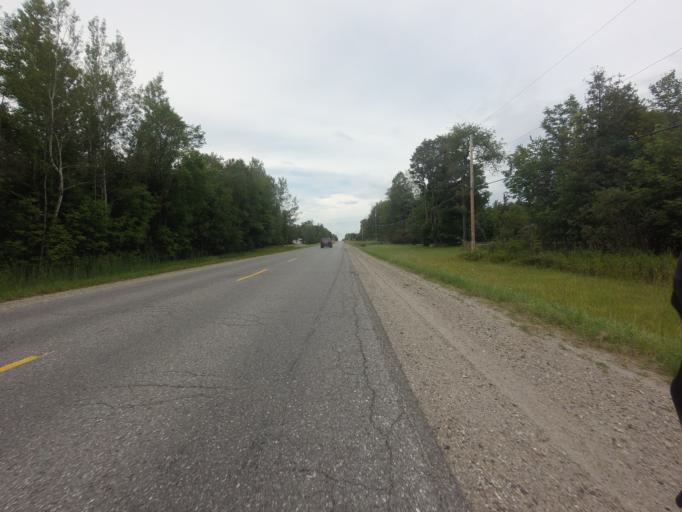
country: CA
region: Ontario
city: Carleton Place
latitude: 45.1418
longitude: -76.3243
